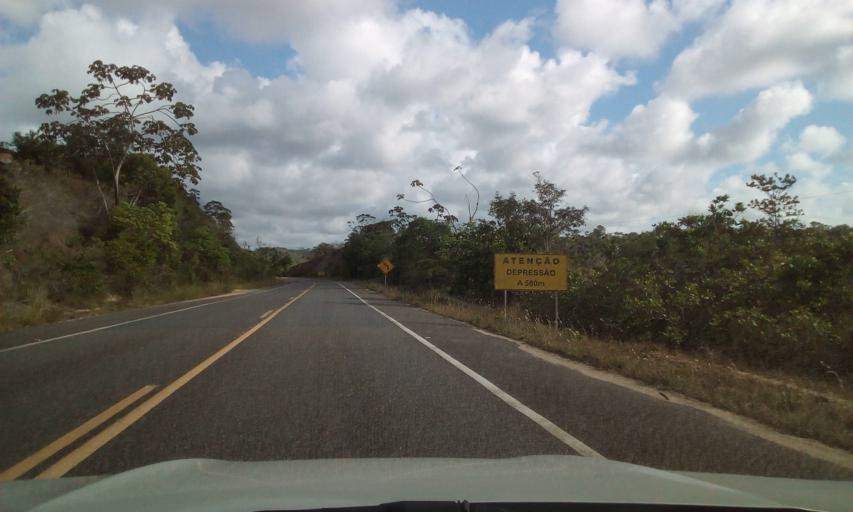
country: BR
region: Bahia
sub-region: Conde
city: Conde
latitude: -11.7098
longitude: -37.5728
